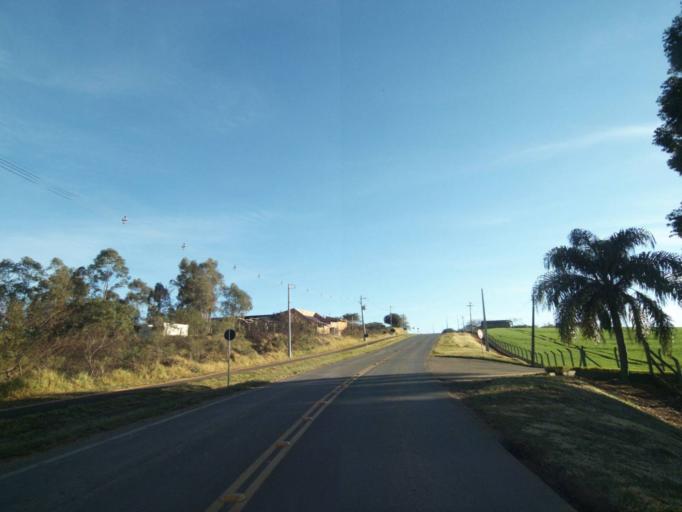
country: BR
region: Parana
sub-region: Tibagi
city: Tibagi
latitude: -24.5208
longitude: -50.4267
